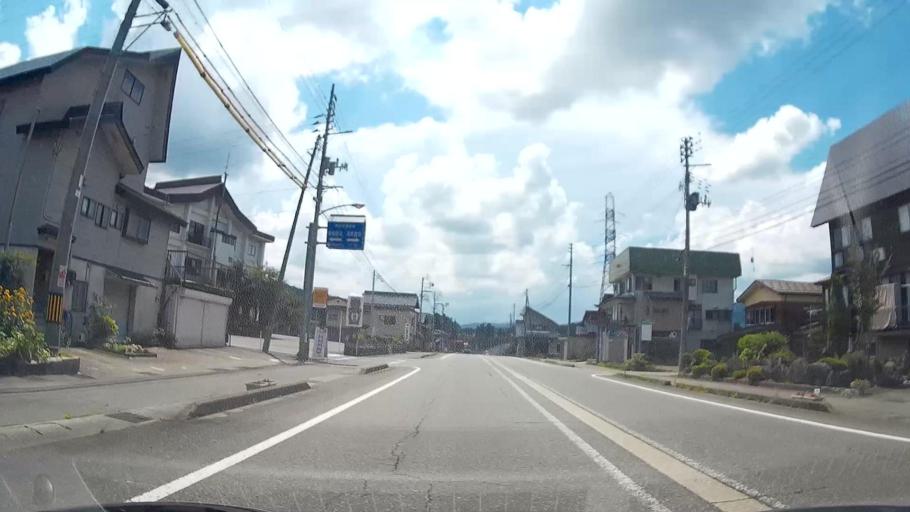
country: JP
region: Niigata
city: Tokamachi
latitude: 37.0482
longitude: 138.6923
